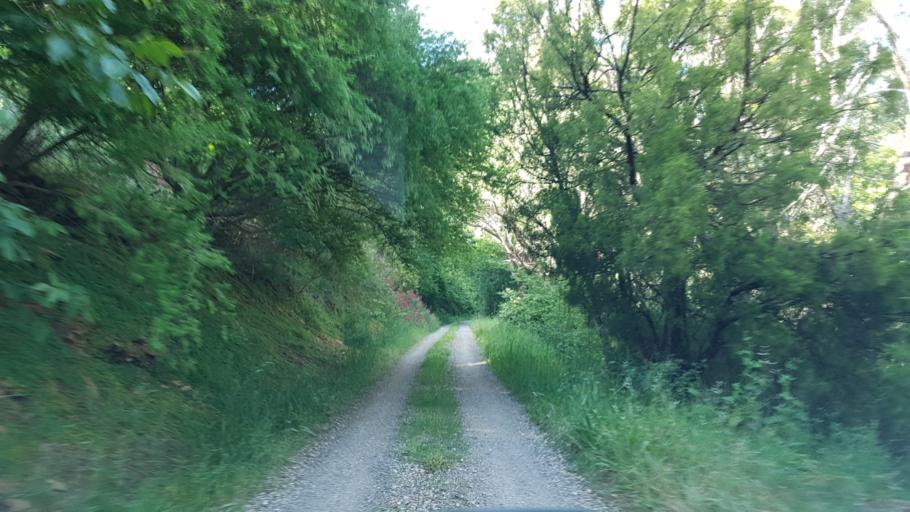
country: AU
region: South Australia
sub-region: Adelaide Hills
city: Adelaide Hills
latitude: -34.9120
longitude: 138.7605
